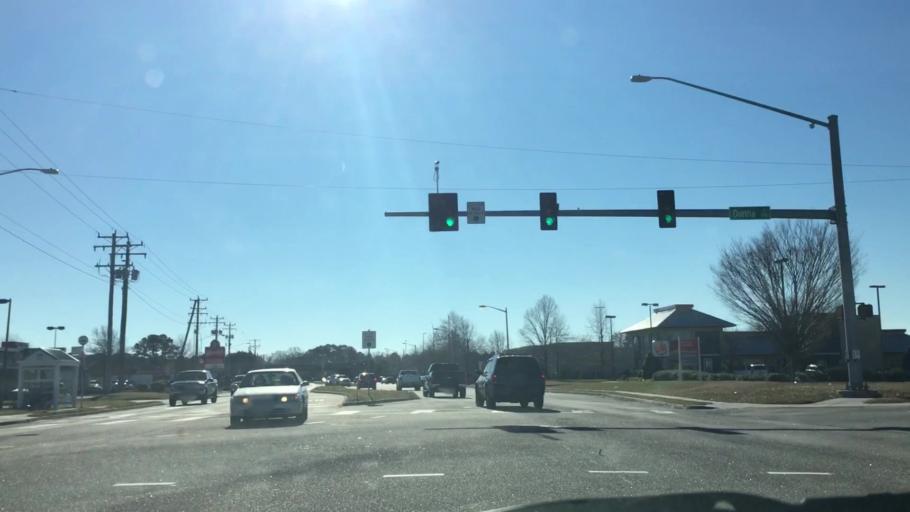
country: US
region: Virginia
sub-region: City of Virginia Beach
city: Virginia Beach
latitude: 36.8486
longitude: -76.0217
